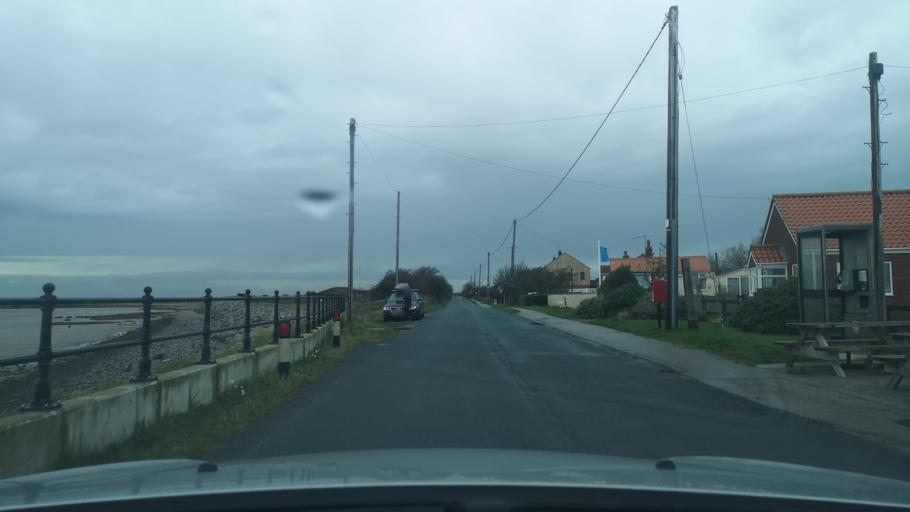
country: GB
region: England
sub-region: East Riding of Yorkshire
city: Easington
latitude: 53.6201
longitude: 0.1294
